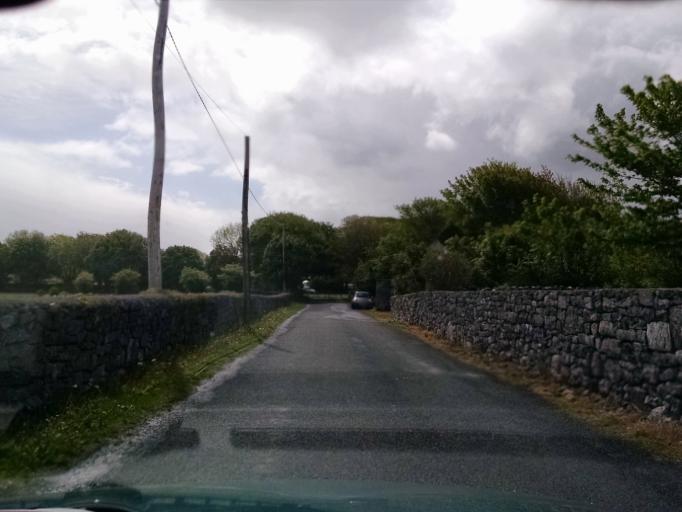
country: IE
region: Connaught
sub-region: County Galway
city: Bearna
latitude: 53.1564
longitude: -9.0850
